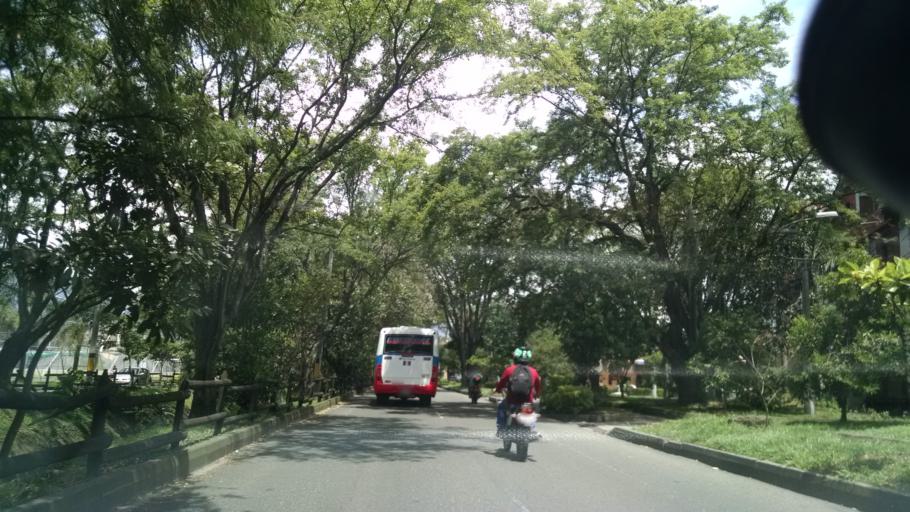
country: CO
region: Antioquia
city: Itagui
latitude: 6.2132
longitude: -75.5865
